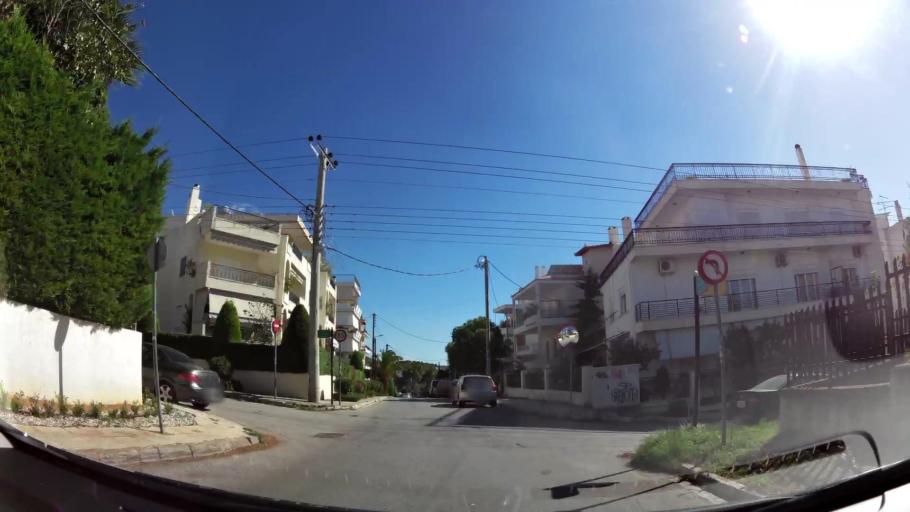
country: GR
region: Attica
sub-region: Nomarchia Anatolikis Attikis
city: Voula
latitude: 37.8382
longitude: 23.7786
